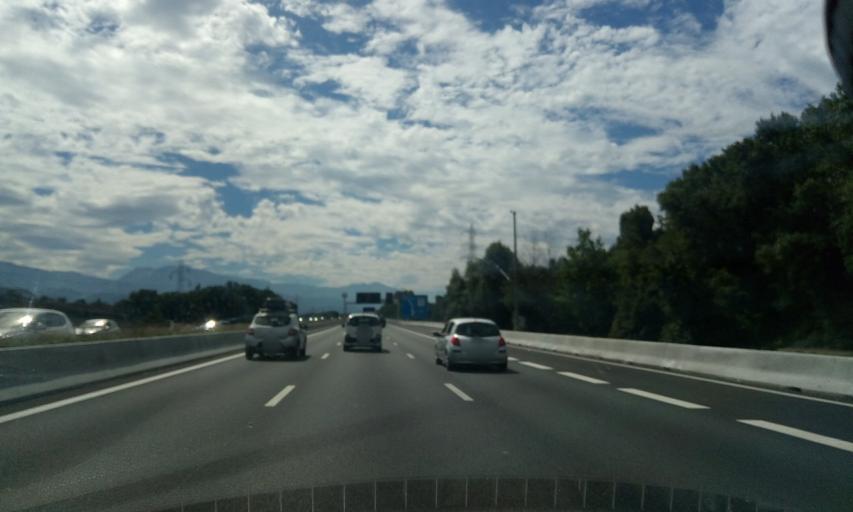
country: FR
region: Rhone-Alpes
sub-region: Departement de l'Isere
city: Saint-Egreve
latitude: 45.2278
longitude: 5.6675
